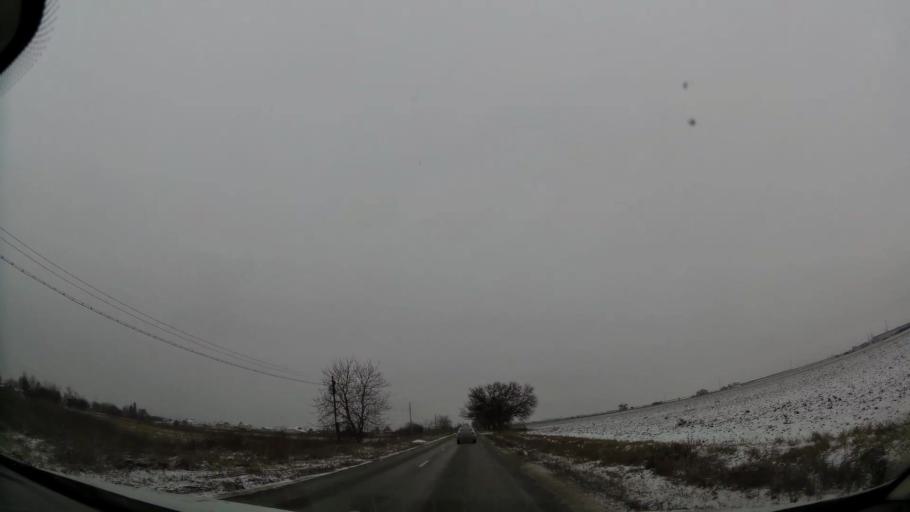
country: RO
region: Dambovita
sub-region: Comuna Ulmi
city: Ulmi
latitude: 44.8914
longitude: 25.5172
